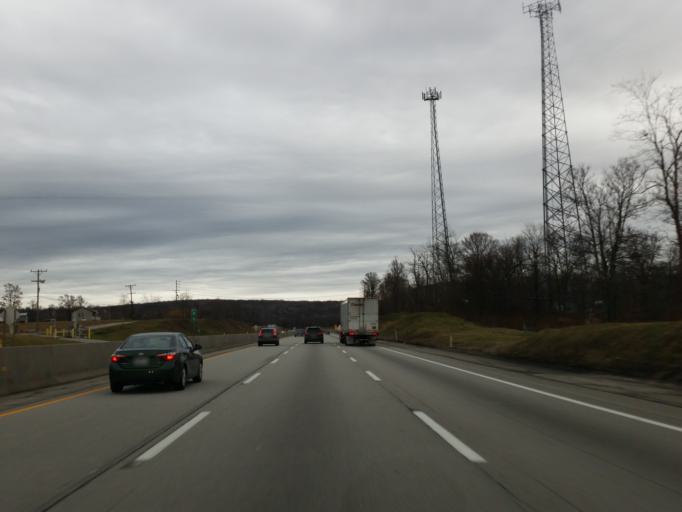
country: US
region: Pennsylvania
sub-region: Westmoreland County
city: Ligonier
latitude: 40.1281
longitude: -79.2887
